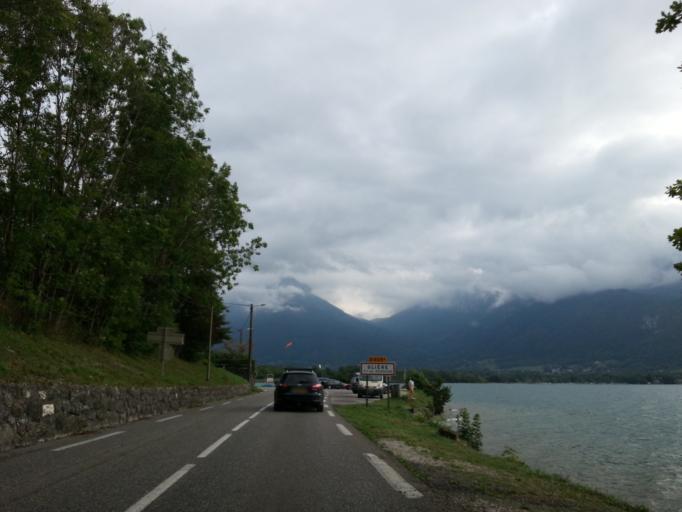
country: FR
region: Rhone-Alpes
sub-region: Departement de la Haute-Savoie
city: Doussard
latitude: 45.8019
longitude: 6.2294
